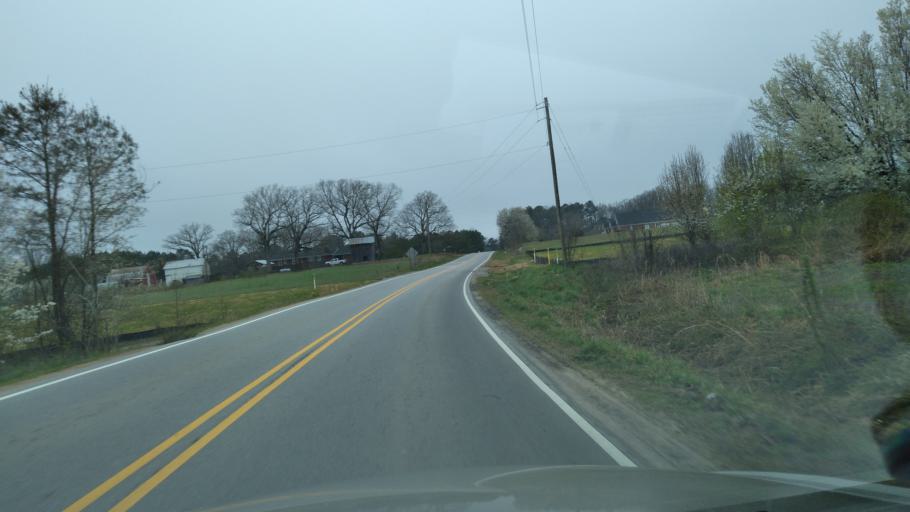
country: US
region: North Carolina
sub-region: Wake County
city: Knightdale
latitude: 35.7426
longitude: -78.4850
